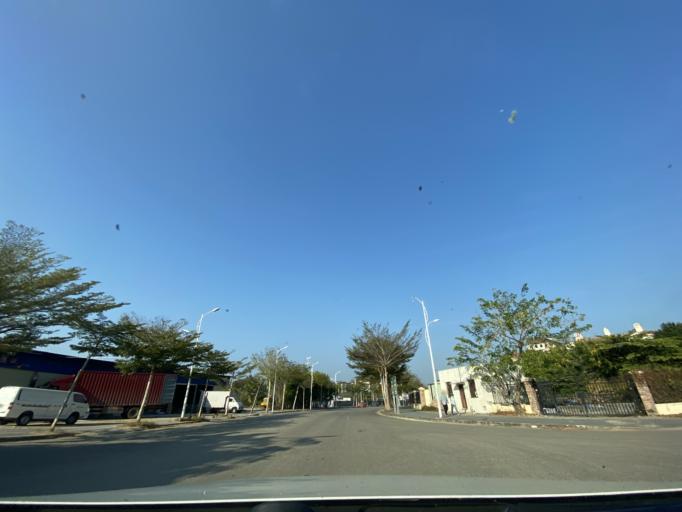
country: CN
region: Hainan
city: Haitangwan
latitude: 18.4105
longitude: 109.7821
